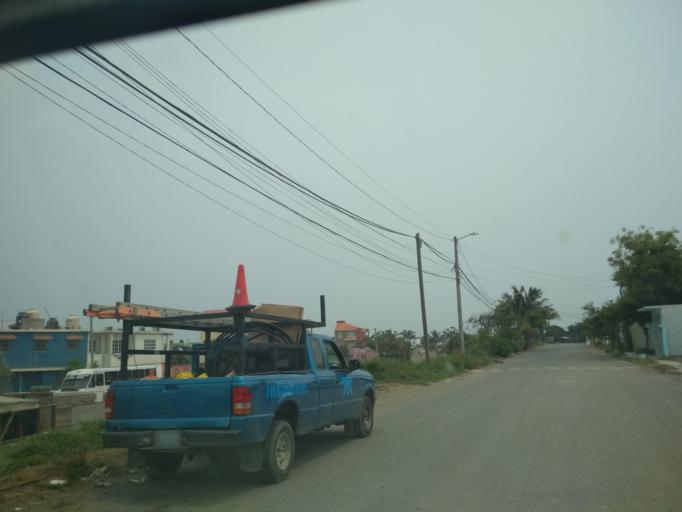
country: MX
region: Veracruz
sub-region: Veracruz
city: Arboledas
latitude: 19.2077
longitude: -96.2148
